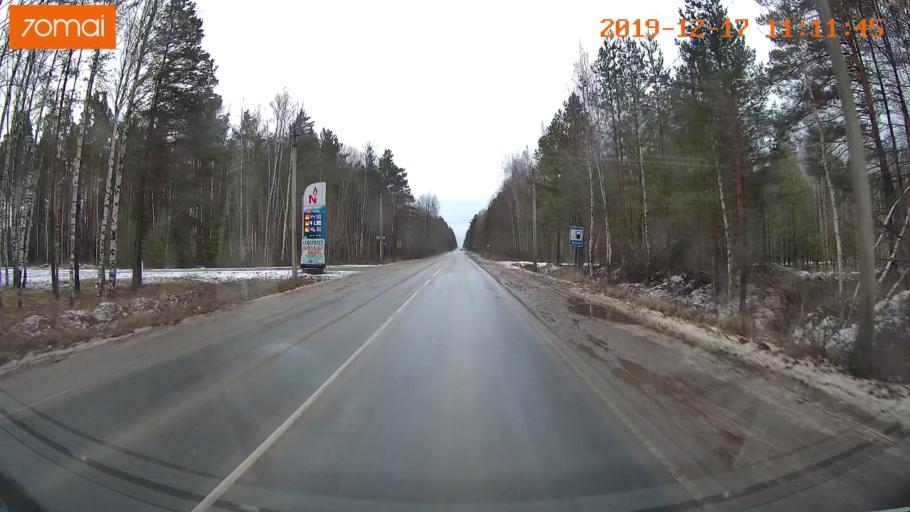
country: RU
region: Vladimir
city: Gus'-Khrustal'nyy
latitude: 55.5841
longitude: 40.6348
